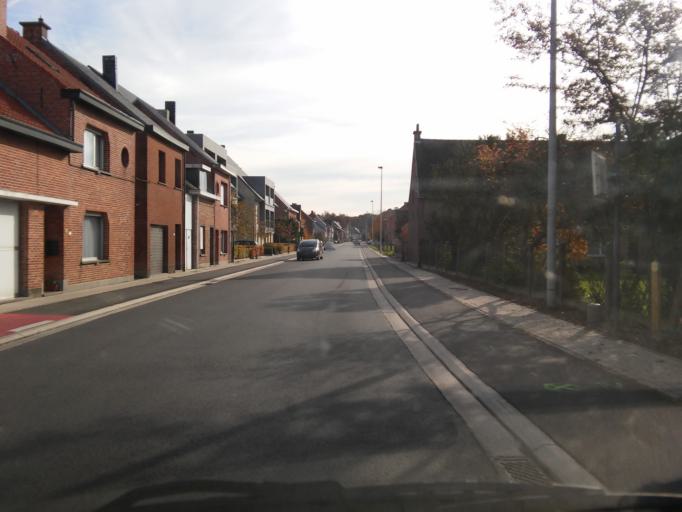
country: BE
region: Flanders
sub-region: Provincie Oost-Vlaanderen
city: Buggenhout
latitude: 51.0100
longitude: 4.2048
